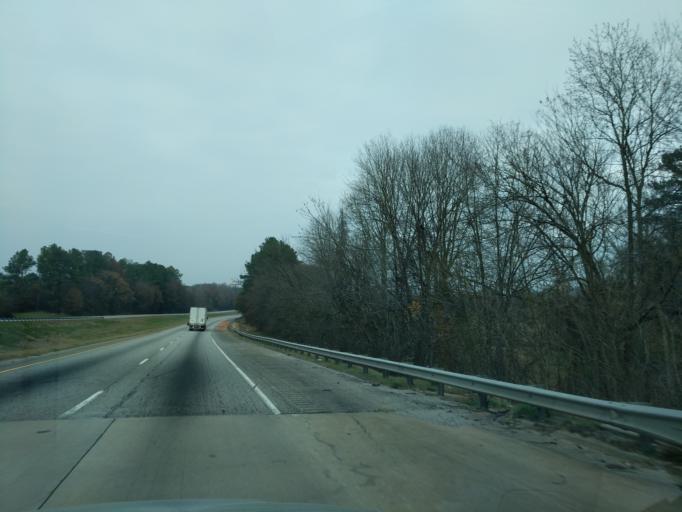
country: US
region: Georgia
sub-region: Franklin County
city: Carnesville
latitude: 34.3594
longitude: -83.2972
